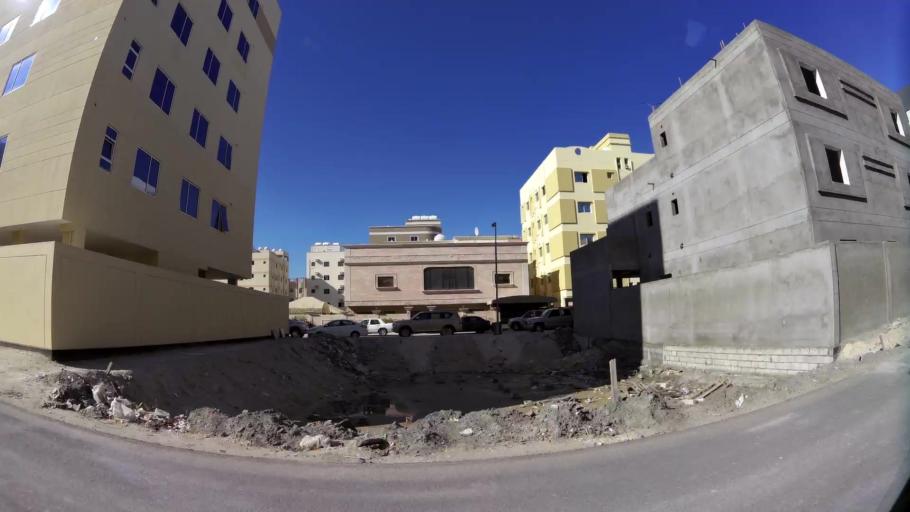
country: BH
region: Muharraq
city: Al Hadd
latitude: 26.2405
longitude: 50.6461
